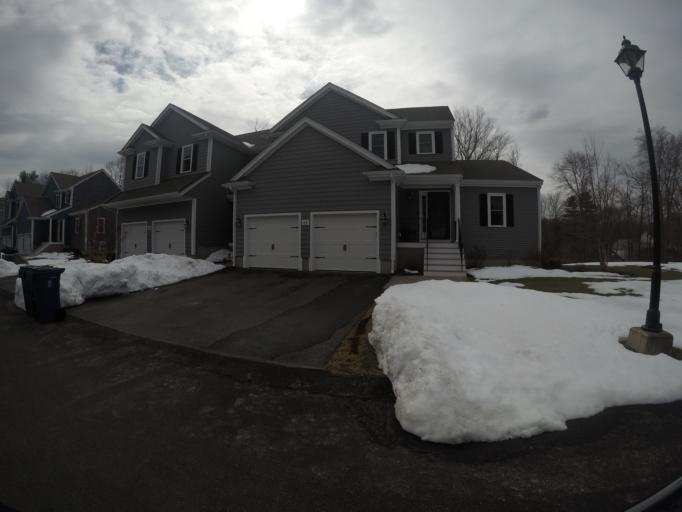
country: US
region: Massachusetts
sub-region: Bristol County
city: Easton
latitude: 42.0318
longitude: -71.1248
